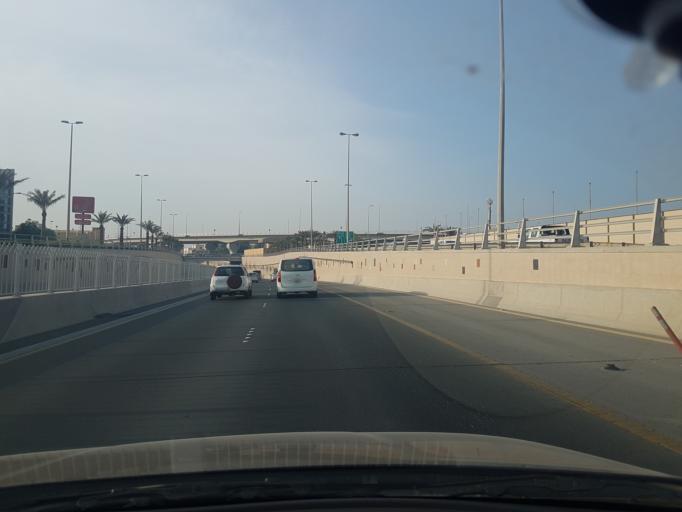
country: BH
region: Northern
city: Madinat `Isa
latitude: 26.1664
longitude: 50.5431
